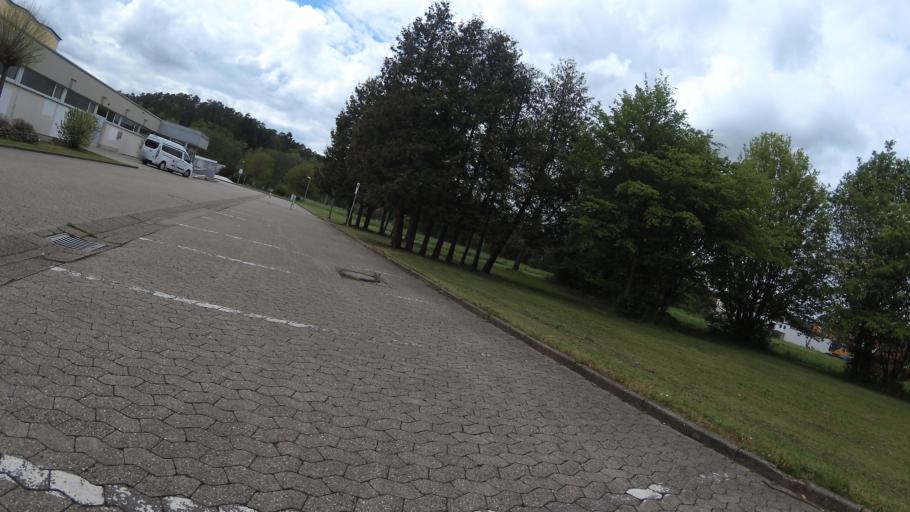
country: DE
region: Saarland
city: Schmelz
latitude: 49.4369
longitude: 6.8475
